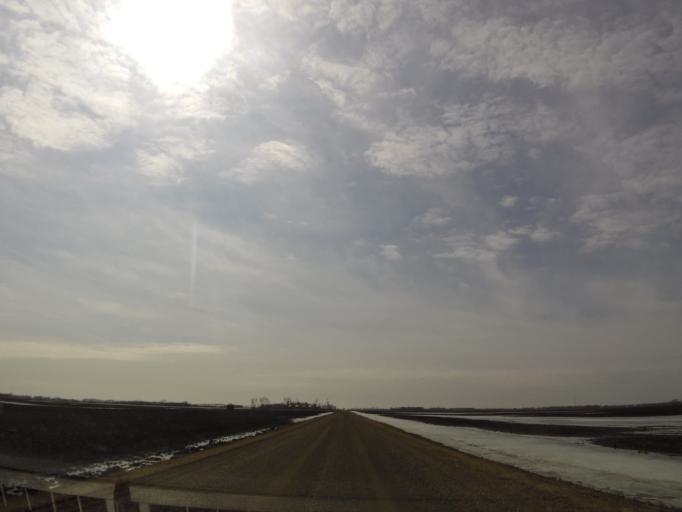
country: US
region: North Dakota
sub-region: Walsh County
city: Grafton
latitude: 48.3304
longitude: -97.2110
